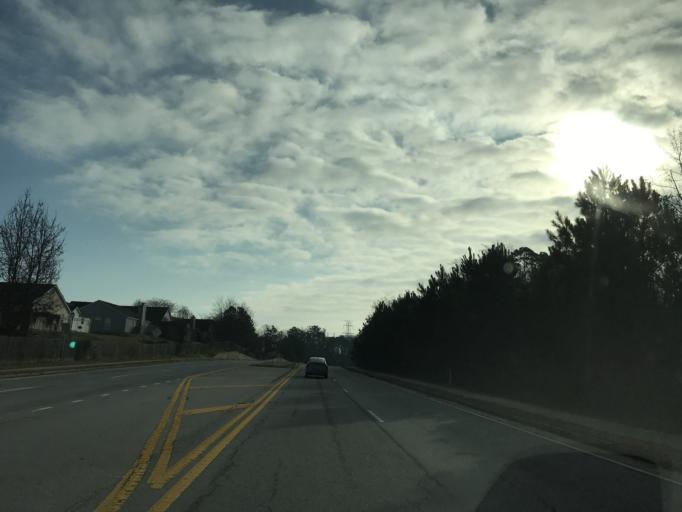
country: US
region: Georgia
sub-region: Clayton County
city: Riverdale
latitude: 33.5927
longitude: -84.4048
